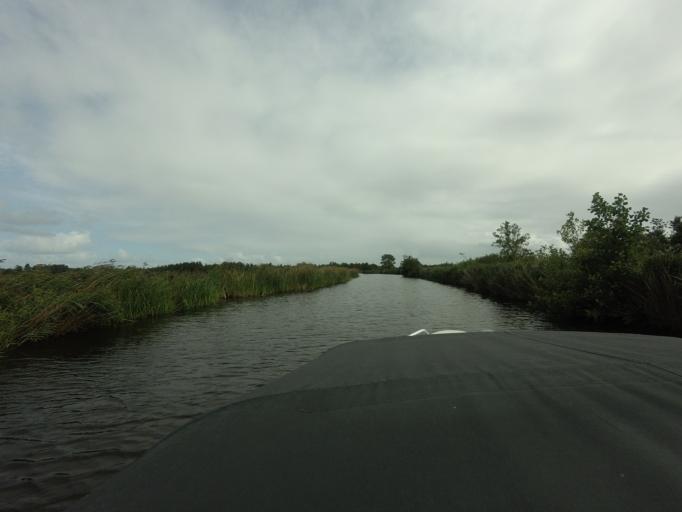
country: NL
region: Friesland
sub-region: Gemeente Boarnsterhim
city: Warten
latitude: 53.1273
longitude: 5.9076
